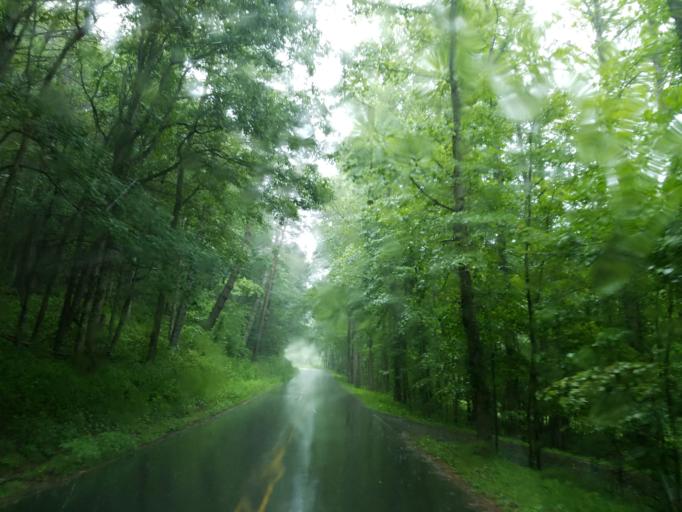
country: US
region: Georgia
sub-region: Fannin County
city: Blue Ridge
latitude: 34.7833
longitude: -84.2926
